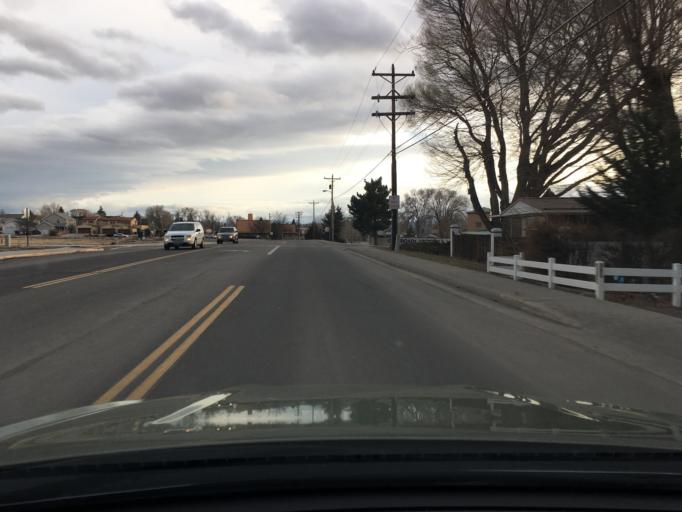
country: US
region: Colorado
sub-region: Montrose County
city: Montrose
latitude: 38.4837
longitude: -107.8571
